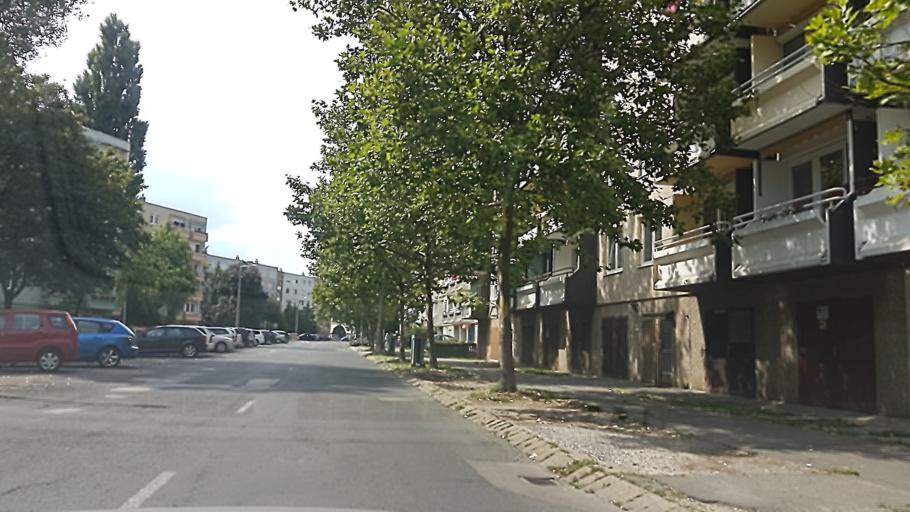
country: HU
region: Gyor-Moson-Sopron
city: Sopron
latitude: 47.6904
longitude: 16.5756
